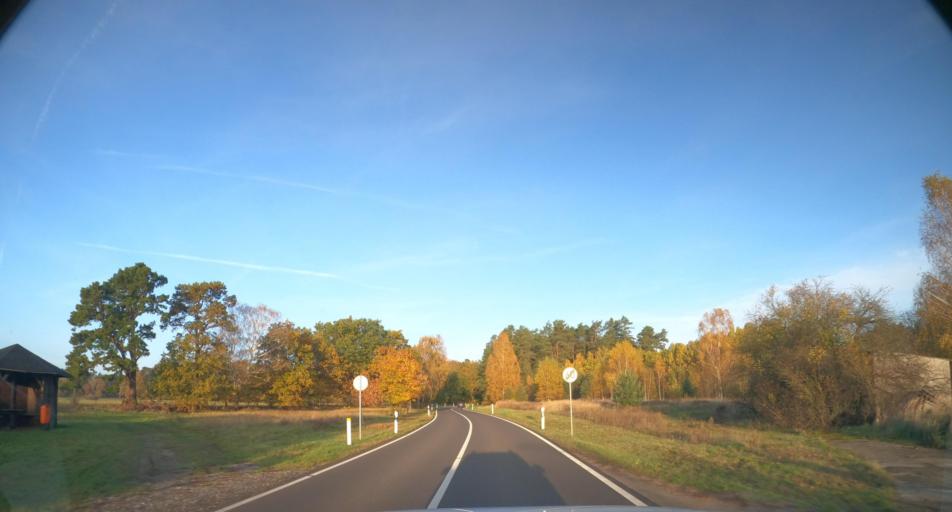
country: DE
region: Mecklenburg-Vorpommern
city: Ahlbeck
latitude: 53.6473
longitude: 14.1942
